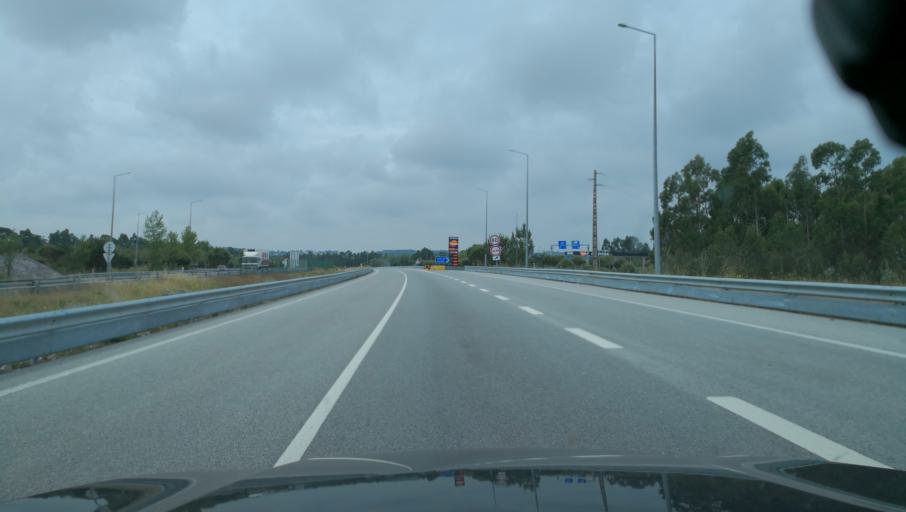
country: PT
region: Coimbra
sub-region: Figueira da Foz
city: Alhadas
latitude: 40.2146
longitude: -8.8091
